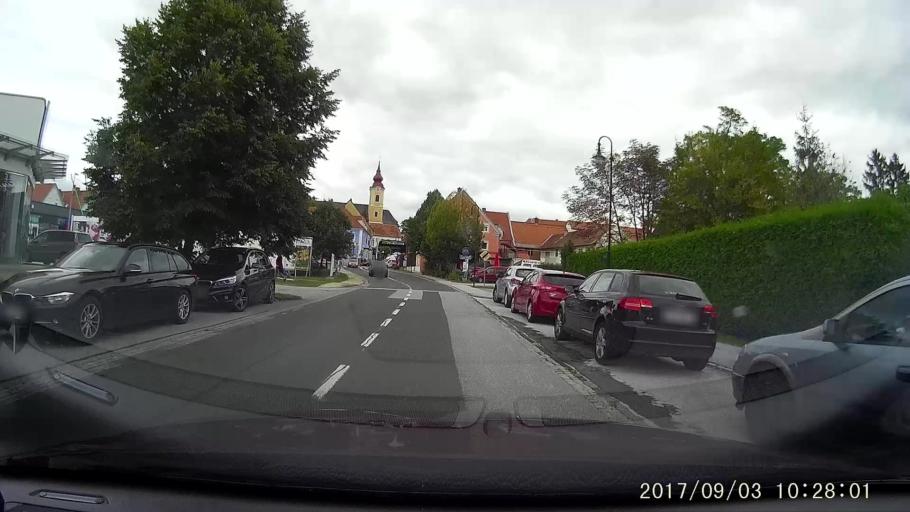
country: AT
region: Styria
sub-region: Politischer Bezirk Hartberg-Fuerstenfeld
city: Ilz
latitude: 47.0855
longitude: 15.9258
